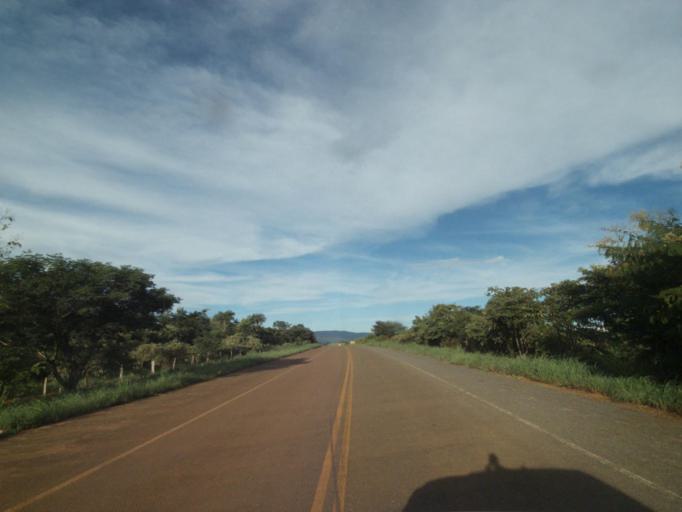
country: BR
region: Goias
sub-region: Jaragua
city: Jaragua
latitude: -15.8673
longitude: -49.4048
